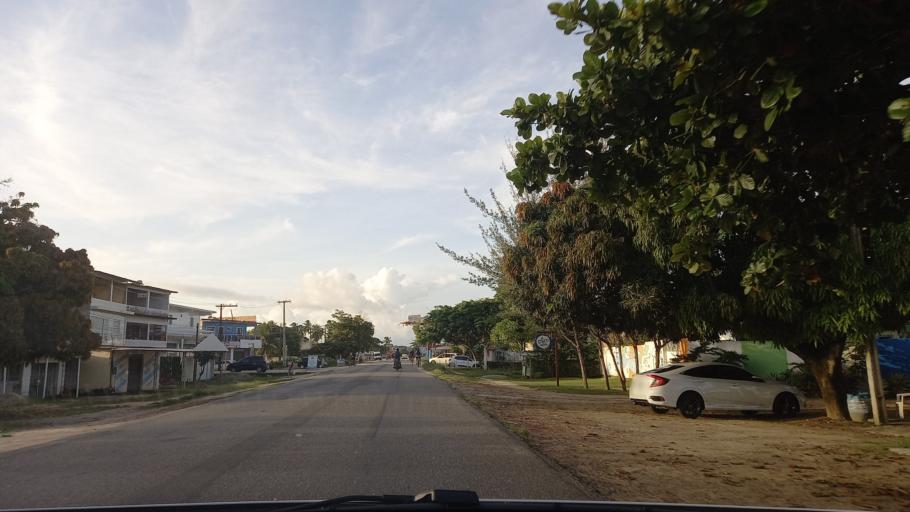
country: BR
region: Pernambuco
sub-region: Sao Jose Da Coroa Grande
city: Sao Jose da Coroa Grande
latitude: -8.9001
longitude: -35.1511
